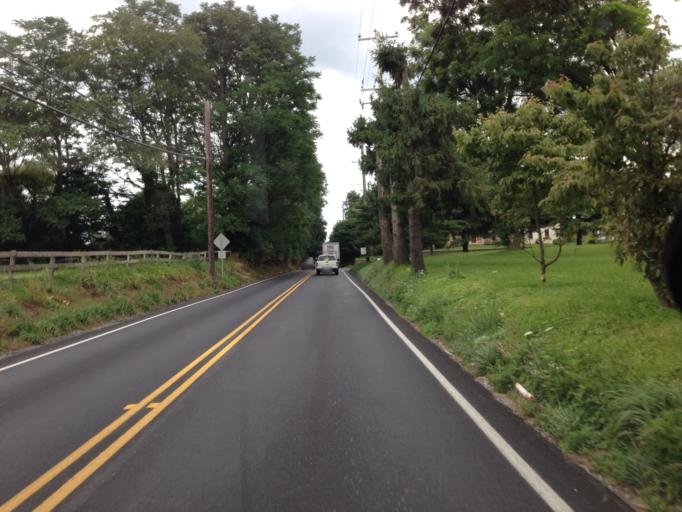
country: US
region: Pennsylvania
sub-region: Chester County
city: West Grove
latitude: 39.7861
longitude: -75.8802
